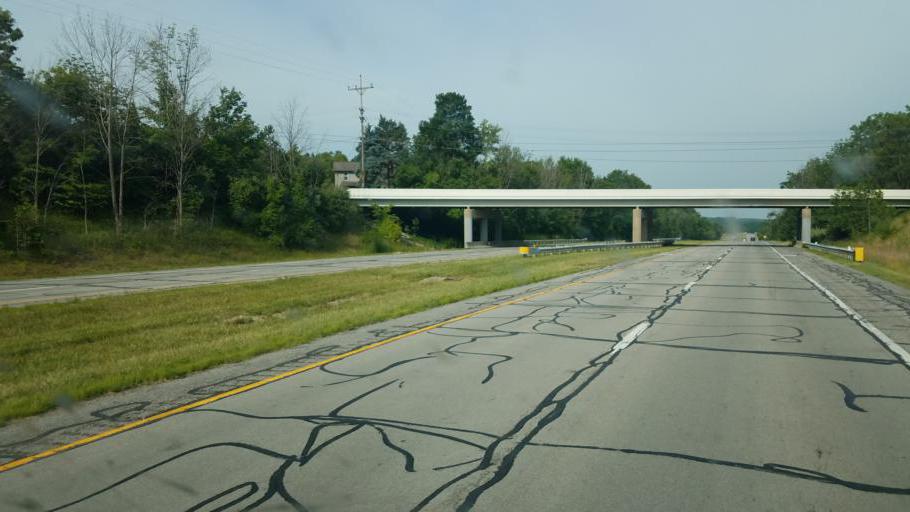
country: US
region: Ohio
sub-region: Medina County
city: Lodi
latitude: 41.0458
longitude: -82.0165
